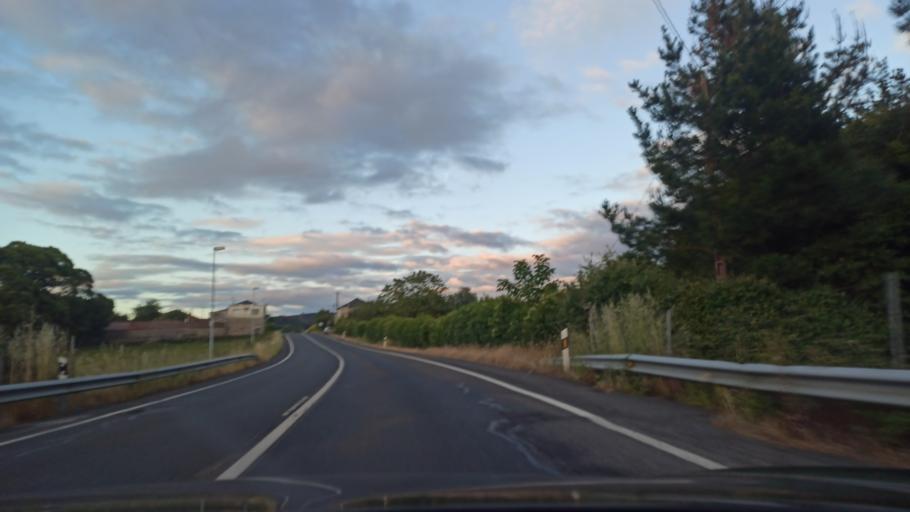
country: ES
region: Galicia
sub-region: Provincia de Lugo
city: Monterroso
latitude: 42.7973
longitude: -7.8070
